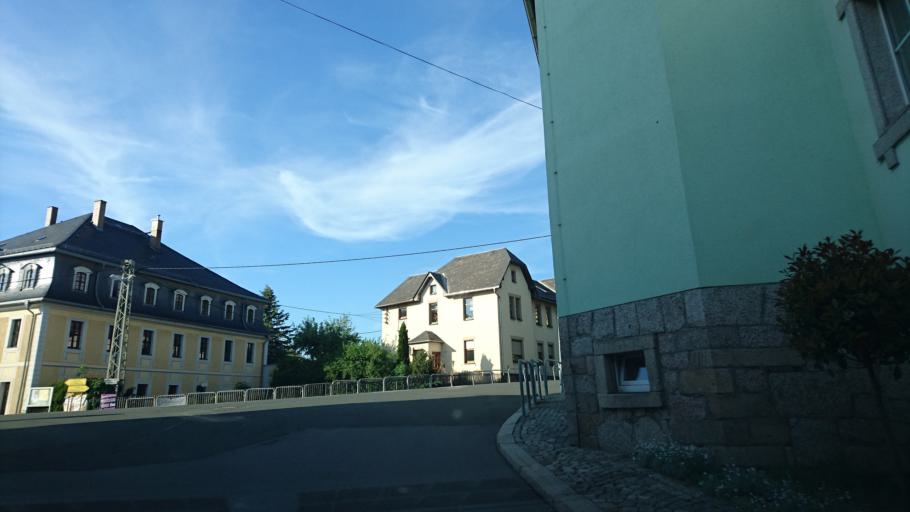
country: DE
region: Saxony
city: Stutzengrun
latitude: 50.5337
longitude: 12.5270
